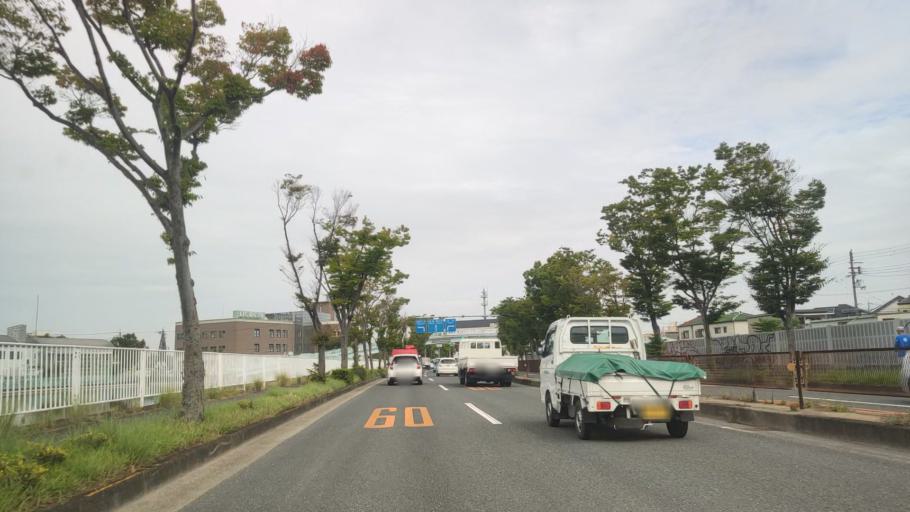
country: JP
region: Osaka
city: Kashihara
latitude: 34.5519
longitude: 135.5998
